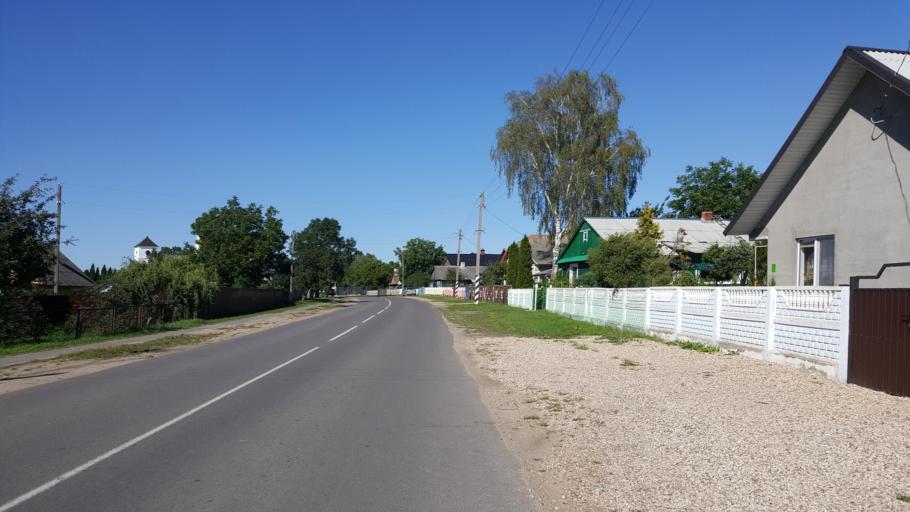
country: BY
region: Brest
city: Charnawchytsy
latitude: 52.2155
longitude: 23.7401
